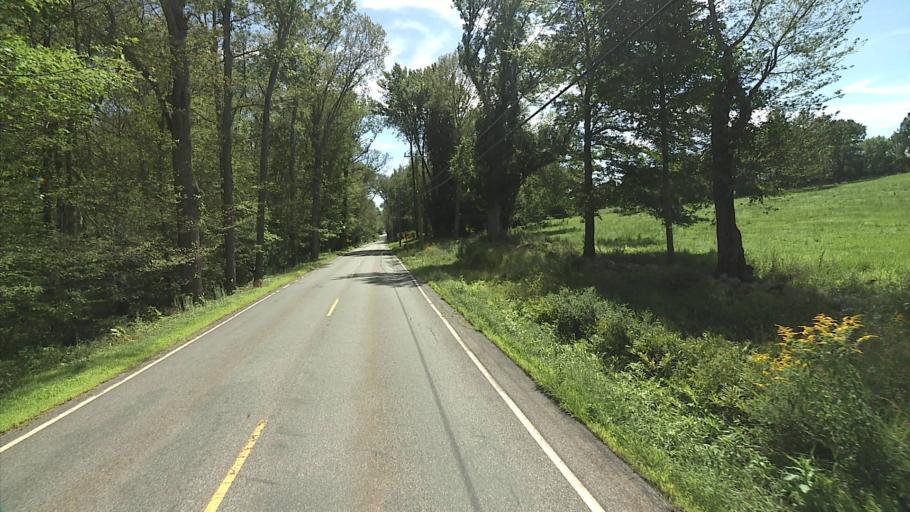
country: US
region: Connecticut
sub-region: Windham County
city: South Woodstock
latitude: 41.8843
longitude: -71.9754
